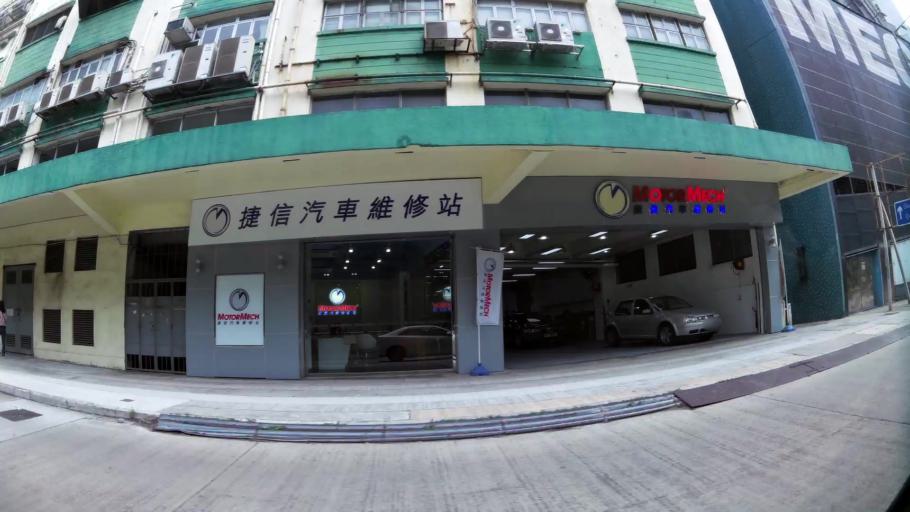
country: HK
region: Wanchai
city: Wan Chai
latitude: 22.2659
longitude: 114.2461
